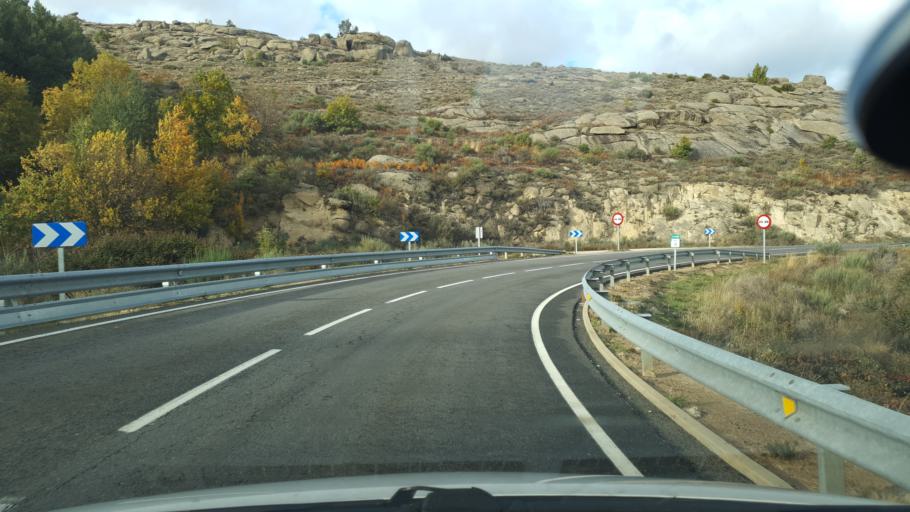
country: ES
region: Castille and Leon
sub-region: Provincia de Avila
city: Navalosa
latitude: 40.3948
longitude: -4.9444
